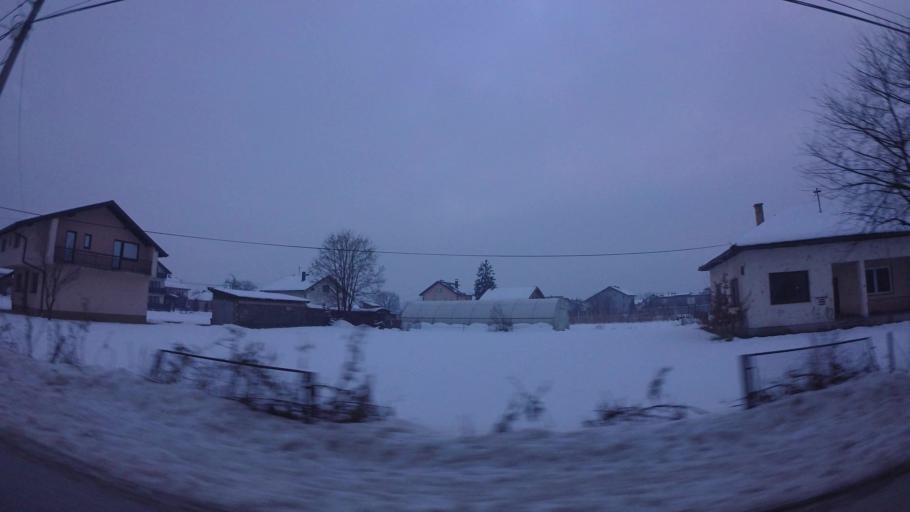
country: BA
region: Federation of Bosnia and Herzegovina
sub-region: Kanton Sarajevo
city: Sarajevo
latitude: 43.8512
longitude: 18.2998
